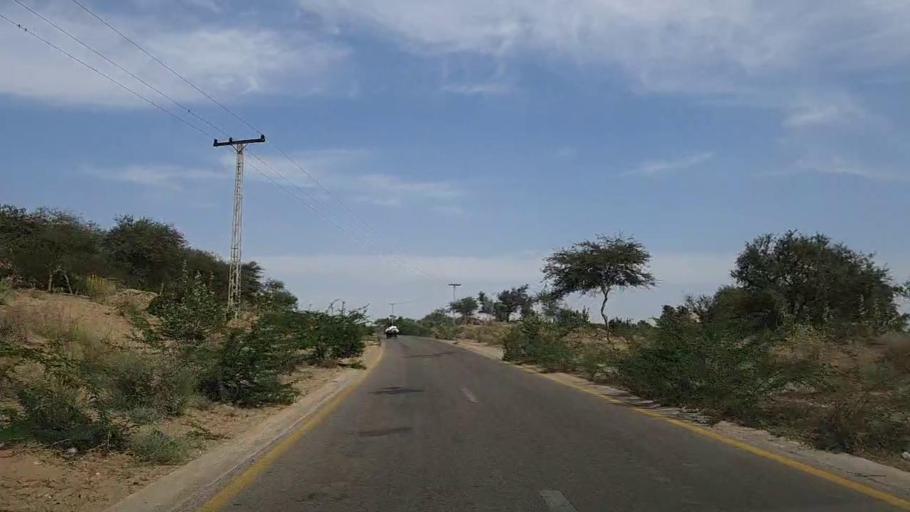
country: PK
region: Sindh
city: Mithi
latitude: 24.7796
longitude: 69.8093
